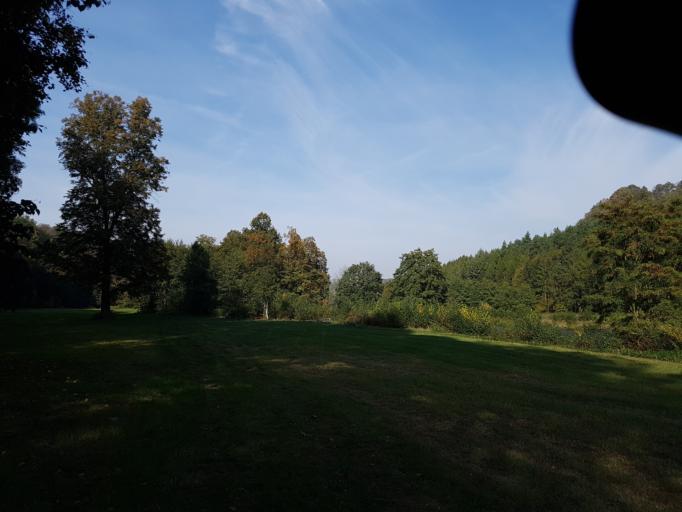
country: DE
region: Saxony
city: Waldheim
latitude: 51.0911
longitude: 13.0256
